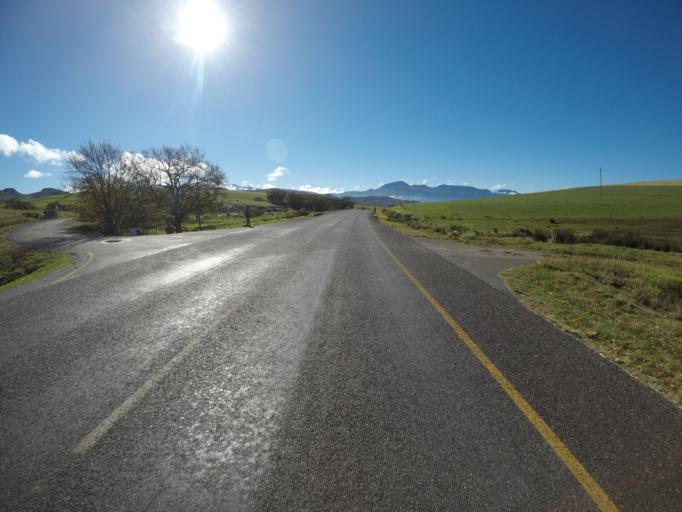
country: ZA
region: Western Cape
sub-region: Overberg District Municipality
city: Caledon
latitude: -34.1255
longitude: 19.5143
